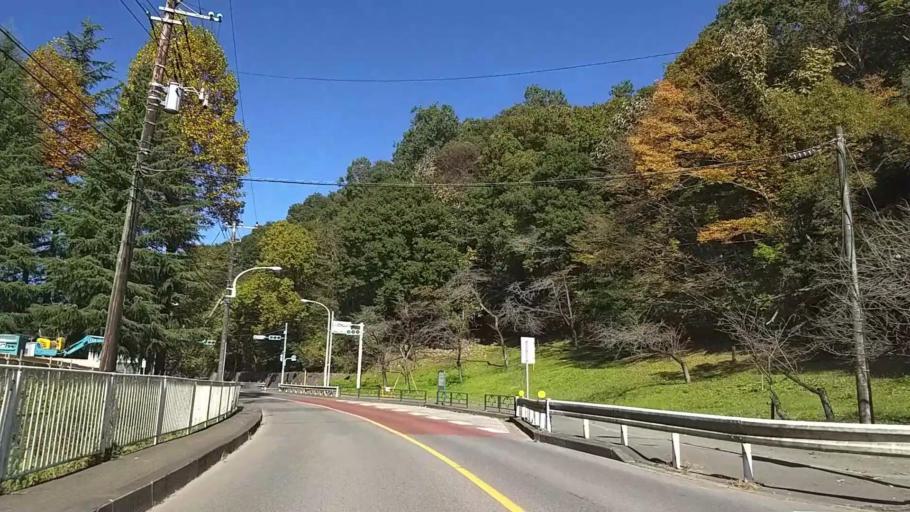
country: JP
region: Tokyo
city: Hachioji
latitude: 35.6172
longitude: 139.2897
